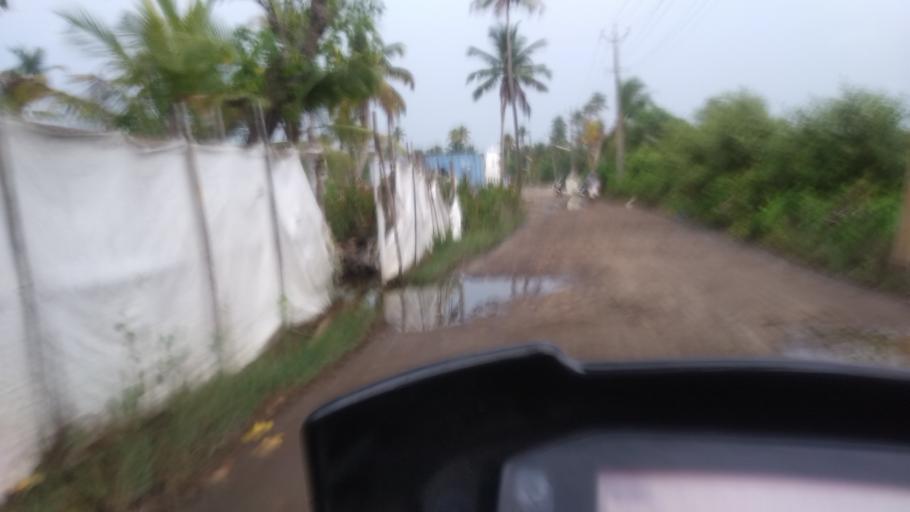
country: IN
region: Kerala
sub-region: Ernakulam
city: Elur
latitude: 10.0683
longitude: 76.2194
